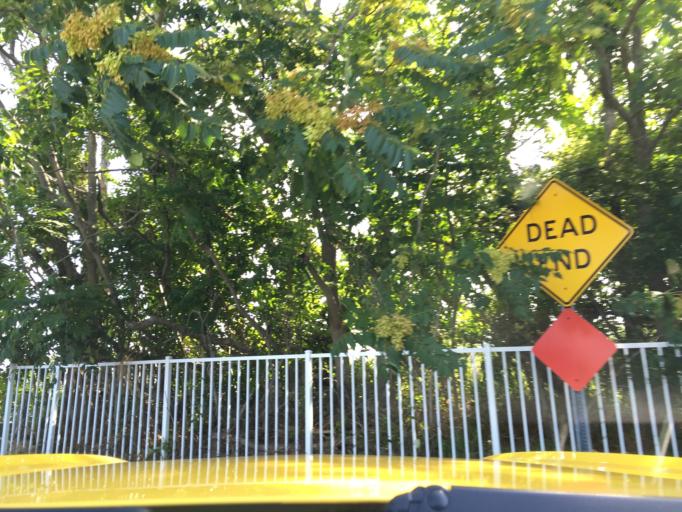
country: US
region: New York
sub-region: Suffolk County
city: Mastic Beach
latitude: 40.7420
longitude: -72.8678
